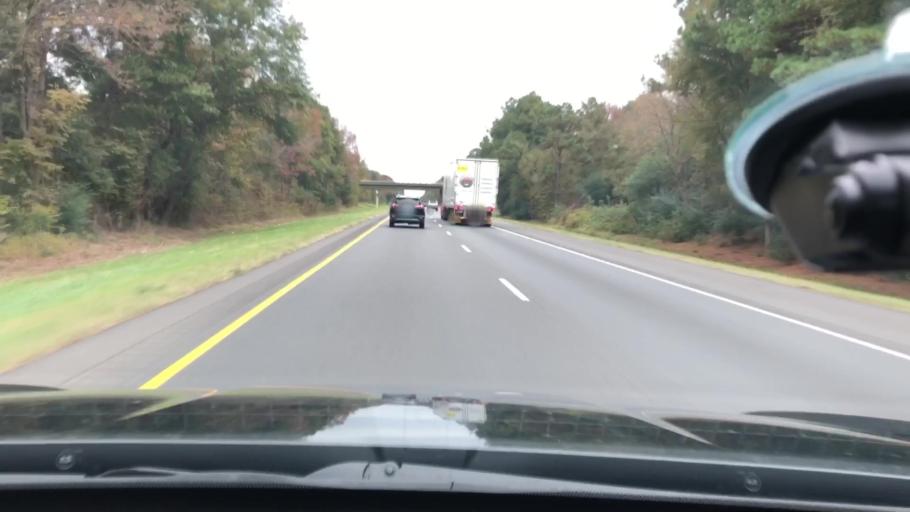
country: US
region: Arkansas
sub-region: Hempstead County
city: Hope
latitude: 33.7016
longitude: -93.5835
